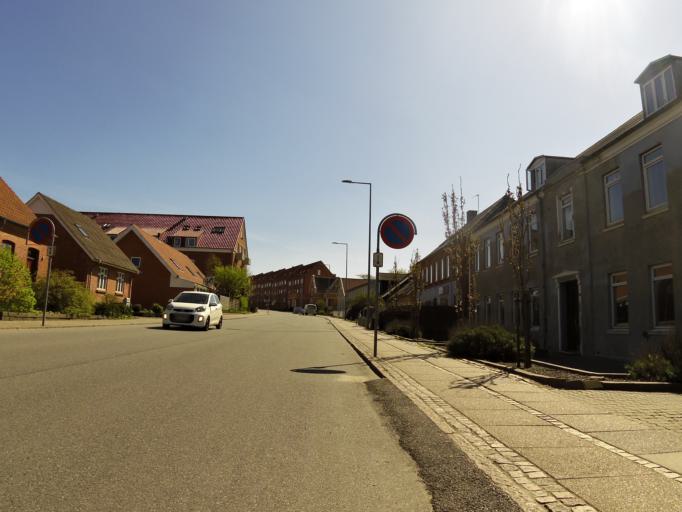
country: DK
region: Central Jutland
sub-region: Struer Kommune
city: Struer
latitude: 56.4896
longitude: 8.5994
